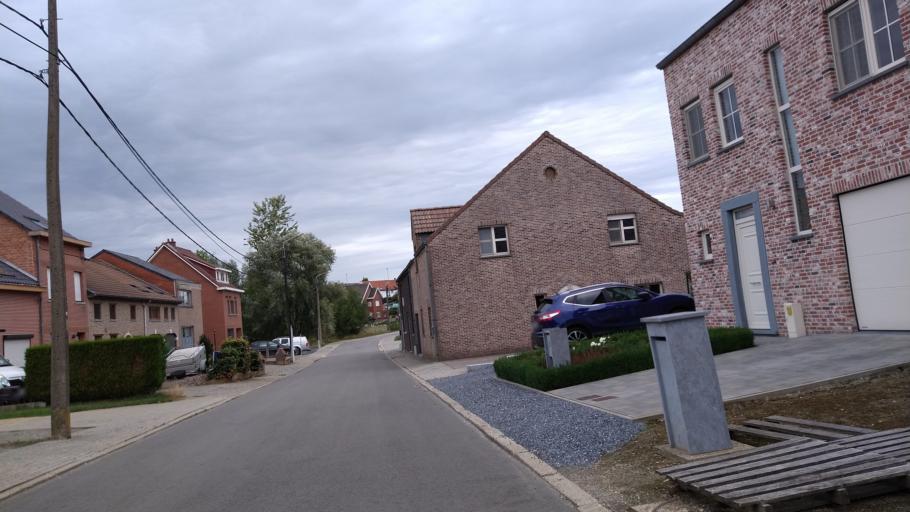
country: BE
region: Flanders
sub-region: Provincie Vlaams-Brabant
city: Bertem
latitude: 50.8551
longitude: 4.5982
